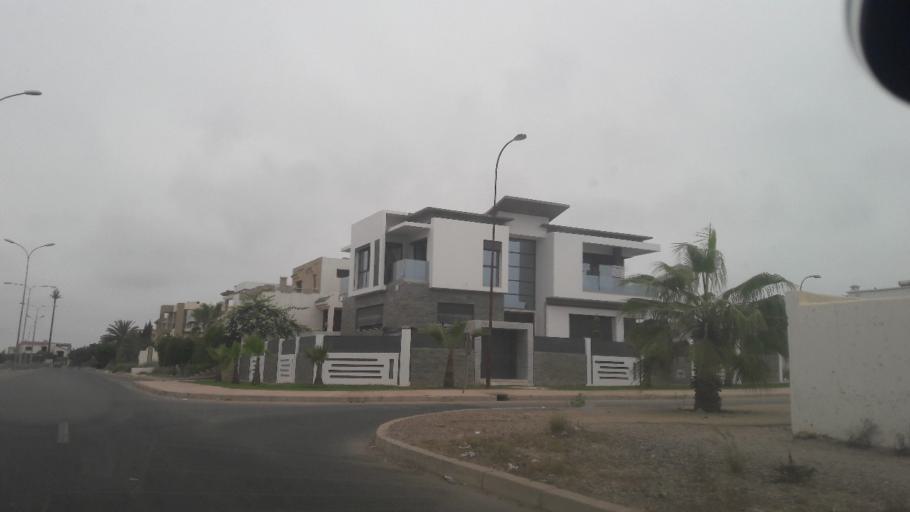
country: MA
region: Souss-Massa-Draa
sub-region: Agadir-Ida-ou-Tnan
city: Agadir
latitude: 30.3893
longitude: -9.5919
